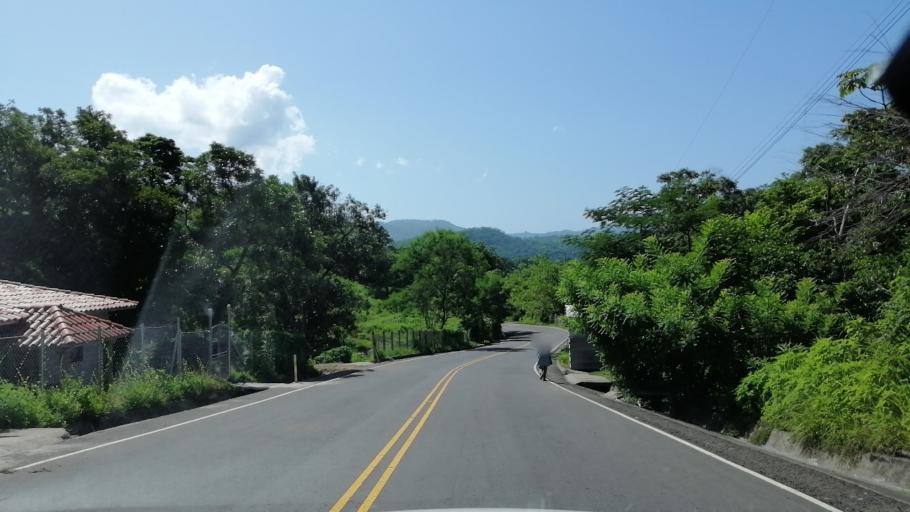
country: SV
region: Cabanas
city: Victoria
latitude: 13.9519
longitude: -88.7382
